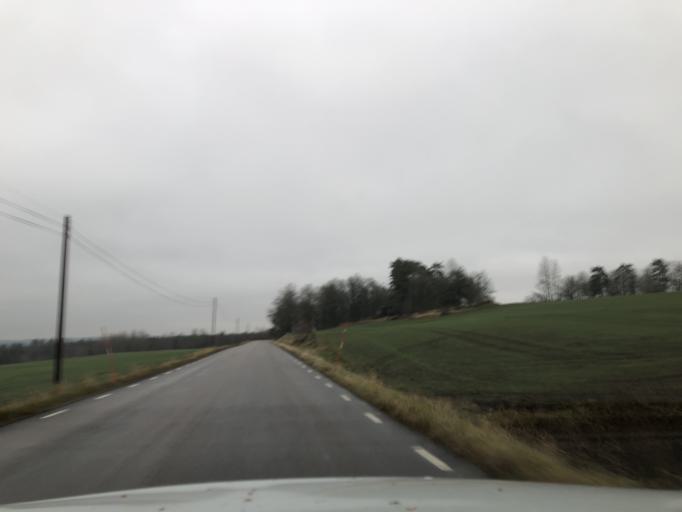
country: SE
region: Vaestra Goetaland
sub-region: Ulricehamns Kommun
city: Ulricehamn
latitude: 57.8497
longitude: 13.3883
